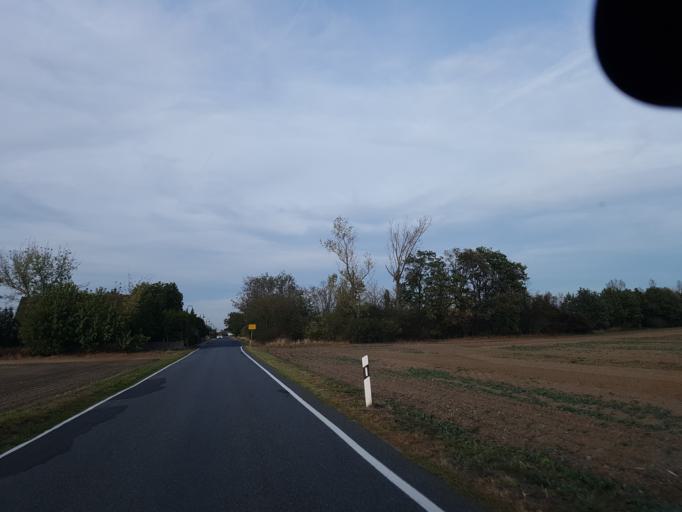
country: DE
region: Saxony
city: Wulknitz
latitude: 51.3521
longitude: 13.3980
